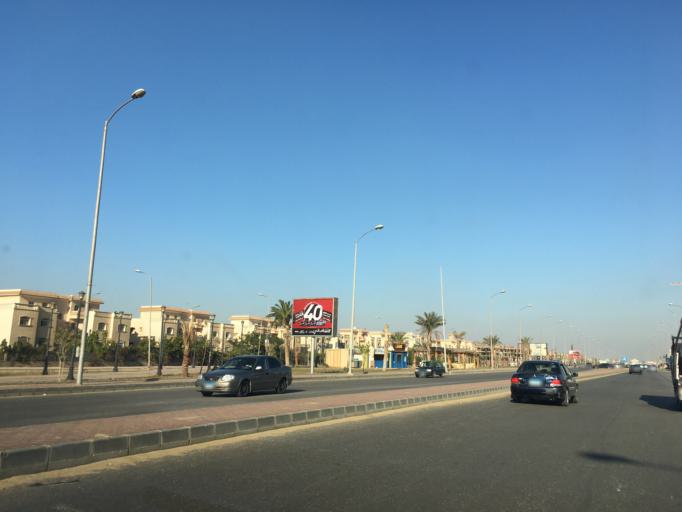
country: EG
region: Al Jizah
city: Madinat Sittah Uktubar
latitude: 30.0042
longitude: 30.9655
